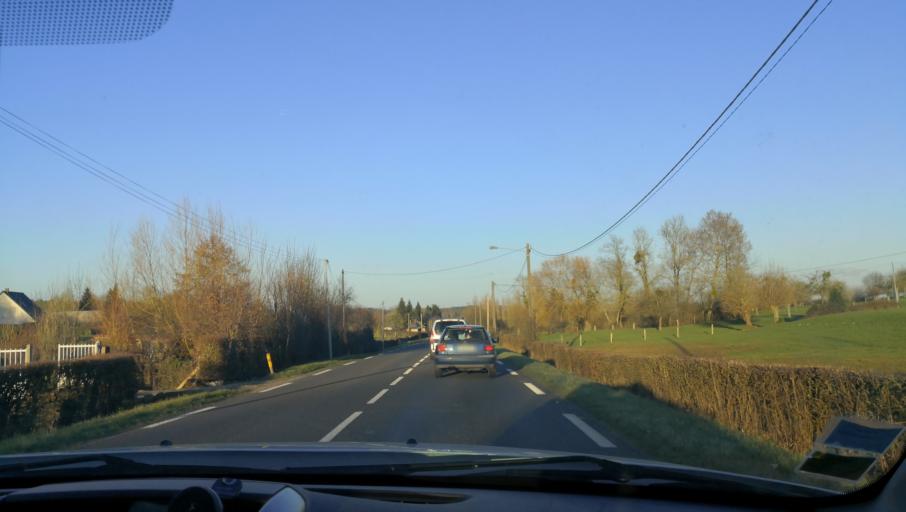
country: FR
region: Haute-Normandie
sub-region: Departement de la Seine-Maritime
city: Forges-les-Eaux
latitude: 49.6006
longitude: 1.4774
